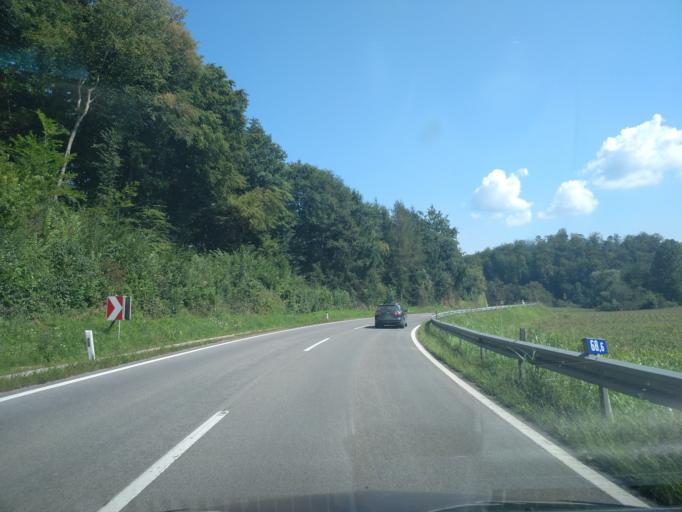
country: AT
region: Styria
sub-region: Politischer Bezirk Leibnitz
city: Ehrenhausen
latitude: 46.7200
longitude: 15.5780
